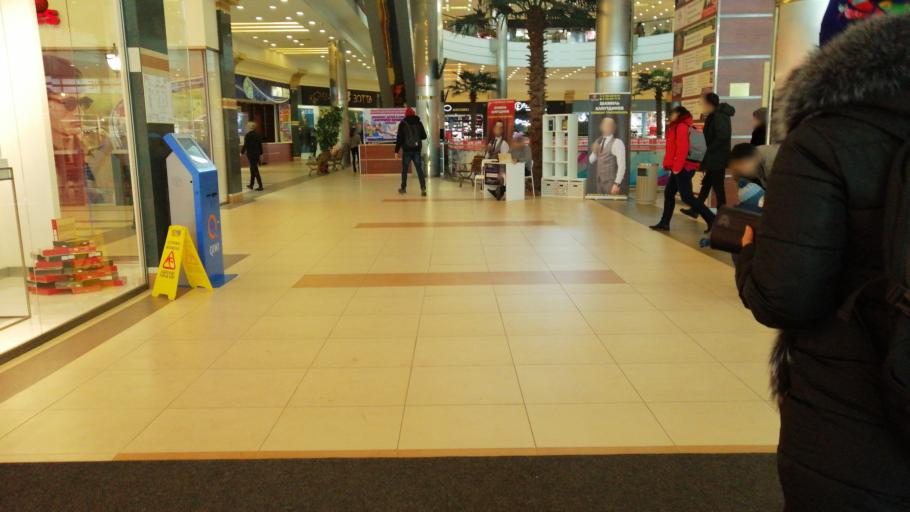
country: KZ
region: Aqtoebe
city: Aqtobe
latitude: 50.2891
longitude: 57.1937
